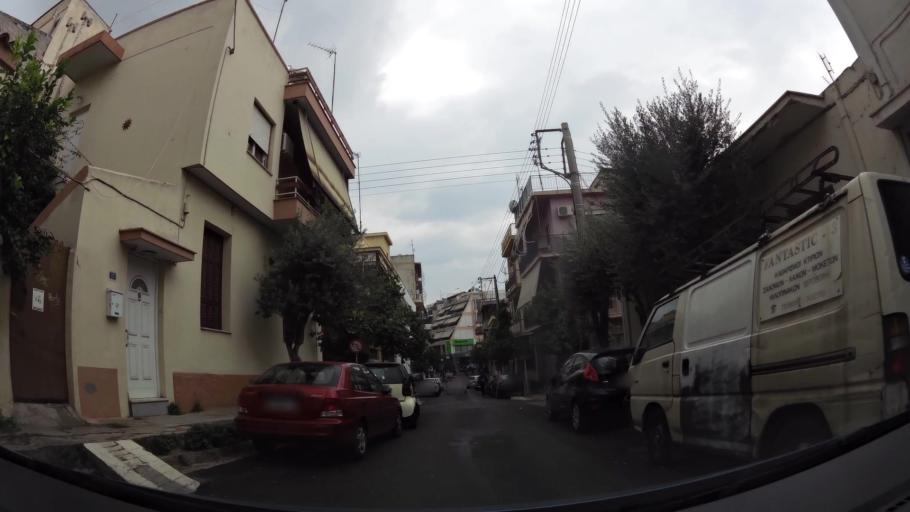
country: GR
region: Attica
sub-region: Nomarchia Athinas
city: Kaisariani
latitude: 37.9611
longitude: 23.7607
